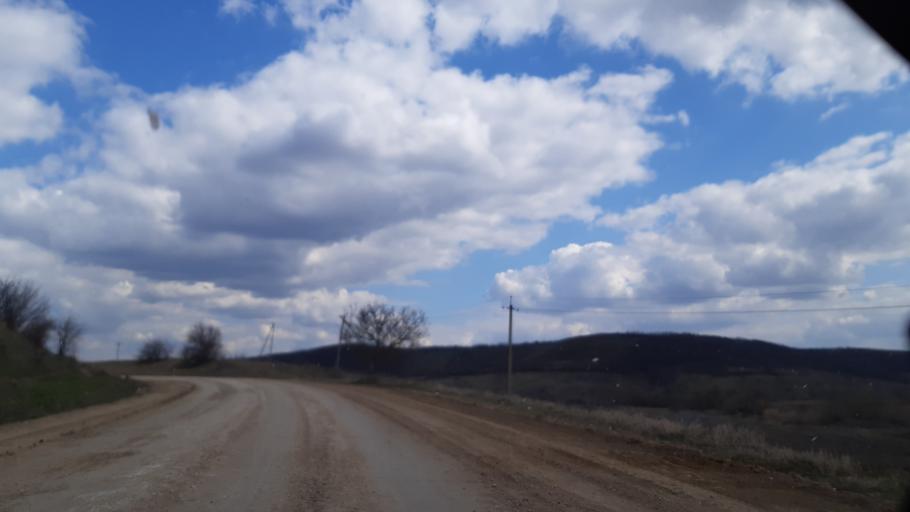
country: MD
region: Laloveni
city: Ialoveni
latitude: 46.8889
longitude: 28.7111
